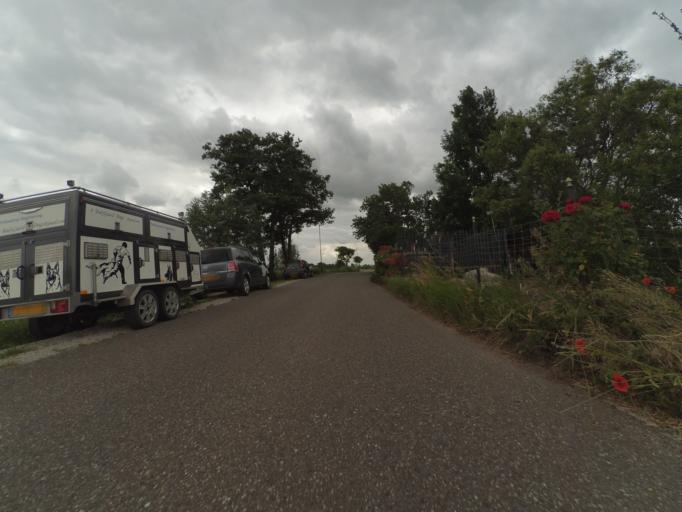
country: NL
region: South Holland
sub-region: Gemeente Giessenlanden
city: Giessenburg
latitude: 51.8651
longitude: 4.9202
